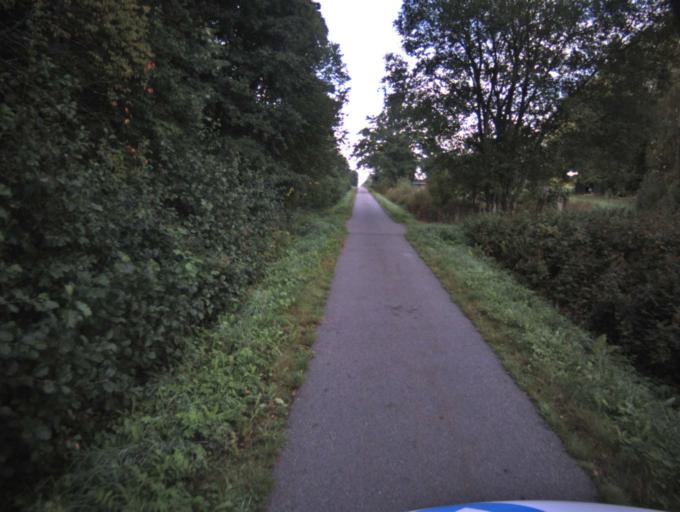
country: SE
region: Vaestra Goetaland
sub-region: Ulricehamns Kommun
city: Ulricehamn
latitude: 57.7678
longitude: 13.4010
